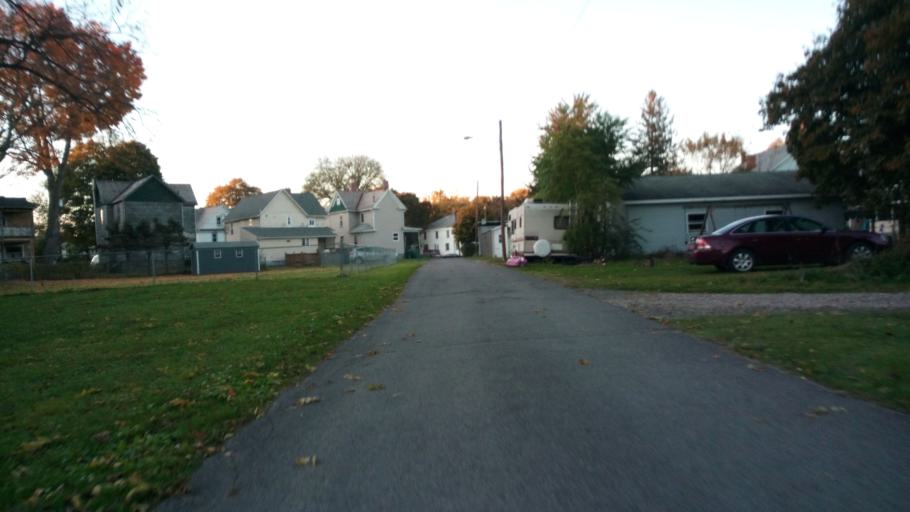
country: US
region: New York
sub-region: Chemung County
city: Elmira
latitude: 42.0795
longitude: -76.8083
